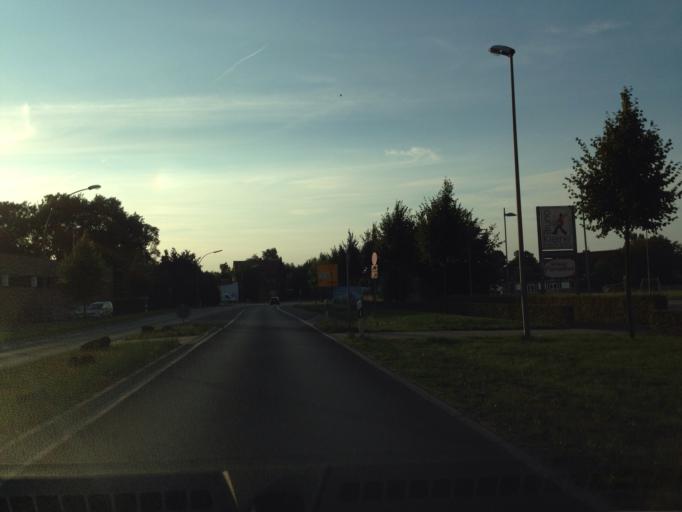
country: DE
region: North Rhine-Westphalia
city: Ludinghausen
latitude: 51.7734
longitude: 7.4494
